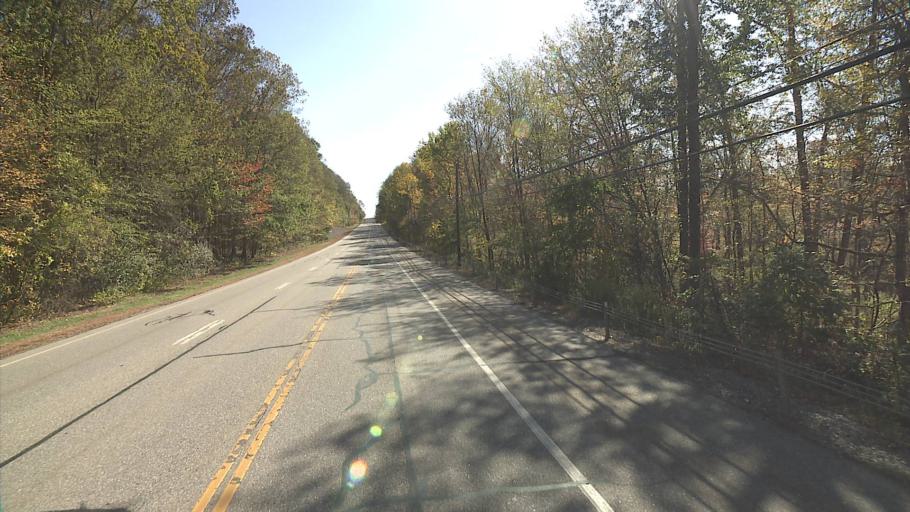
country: US
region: Connecticut
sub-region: Windham County
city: Windham
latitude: 41.7730
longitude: -72.0672
